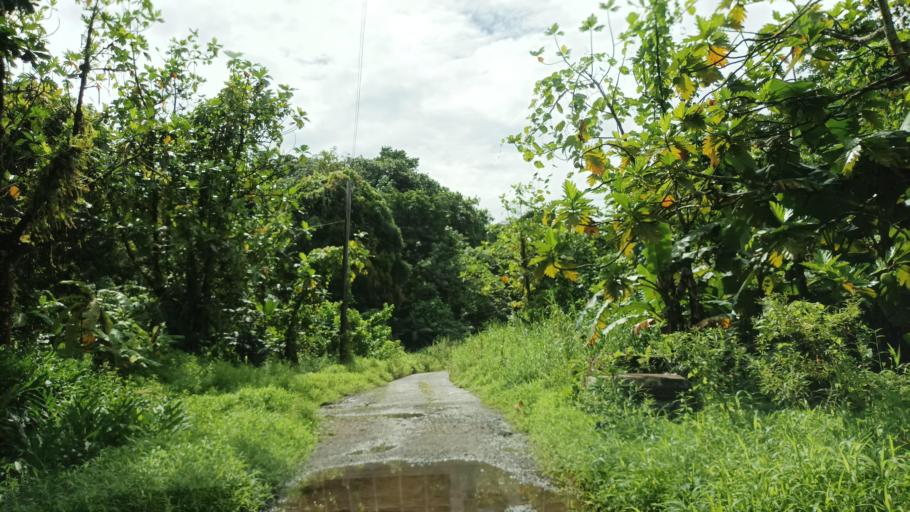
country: FM
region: Kosrae
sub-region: Tafunsak Municipality
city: Tafunsak
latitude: 5.3448
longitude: 162.9752
